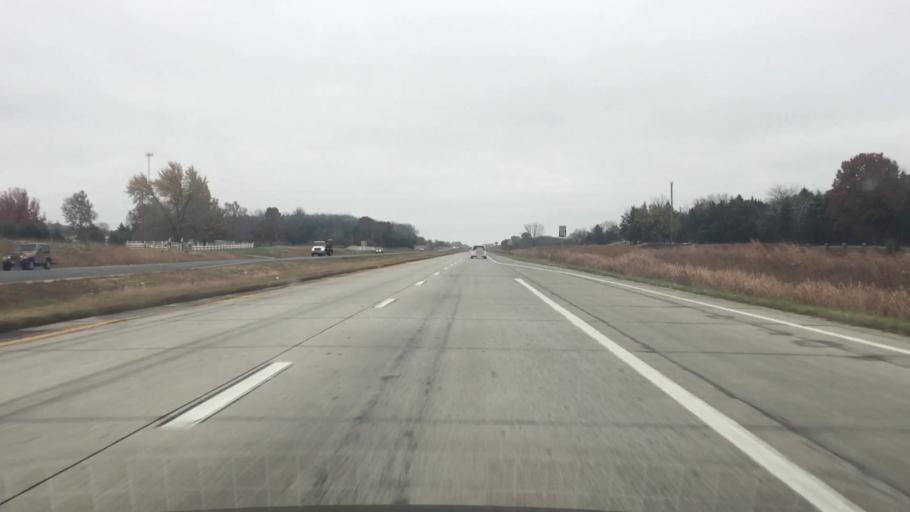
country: US
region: Missouri
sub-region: Saint Clair County
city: Osceola
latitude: 38.0093
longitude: -93.6578
